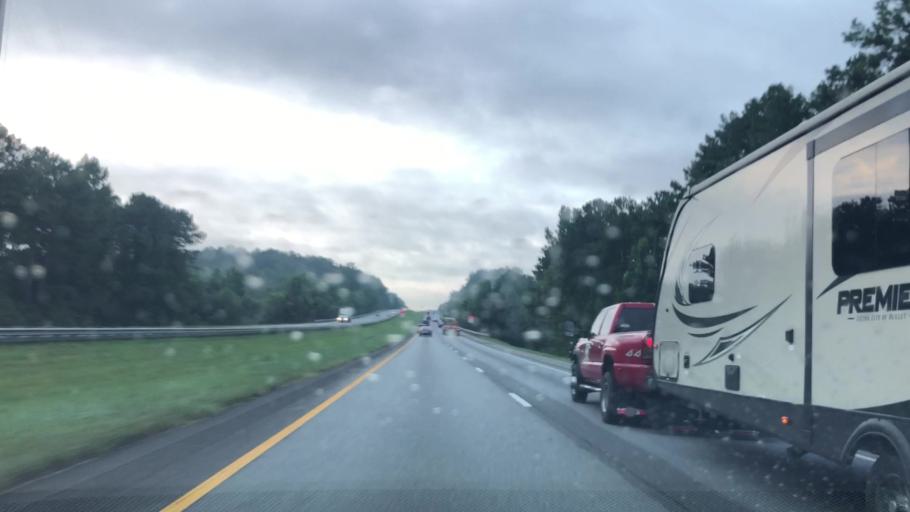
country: US
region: Alabama
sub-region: Shelby County
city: Calera
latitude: 33.0839
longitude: -86.7360
